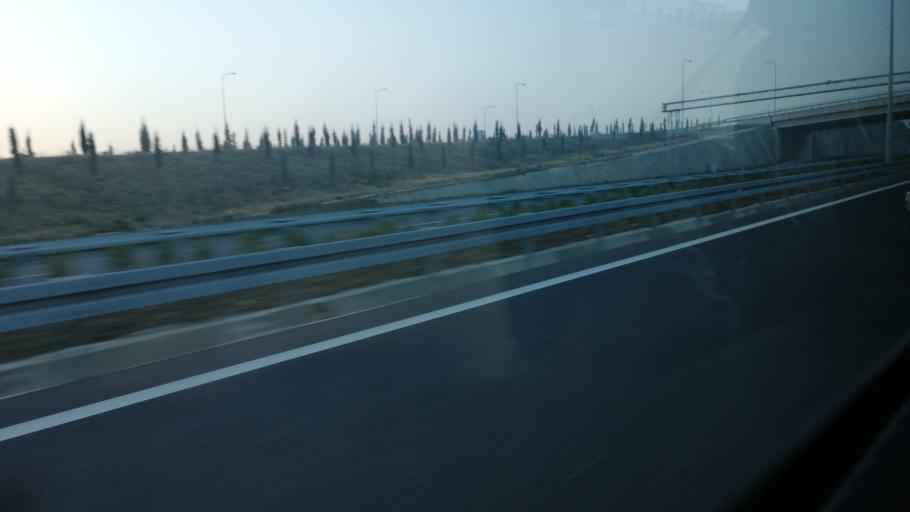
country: TR
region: Kocaeli
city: Tavsanli
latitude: 40.7755
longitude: 29.5185
